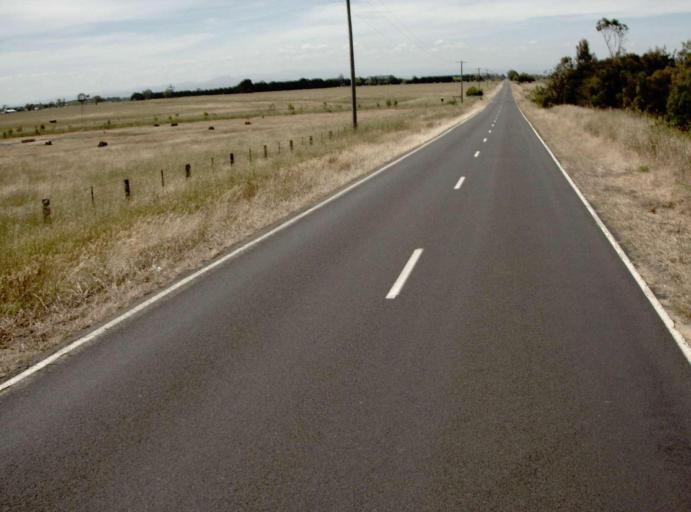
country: AU
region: Victoria
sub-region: Wellington
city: Heyfield
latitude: -38.1104
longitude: 146.8622
